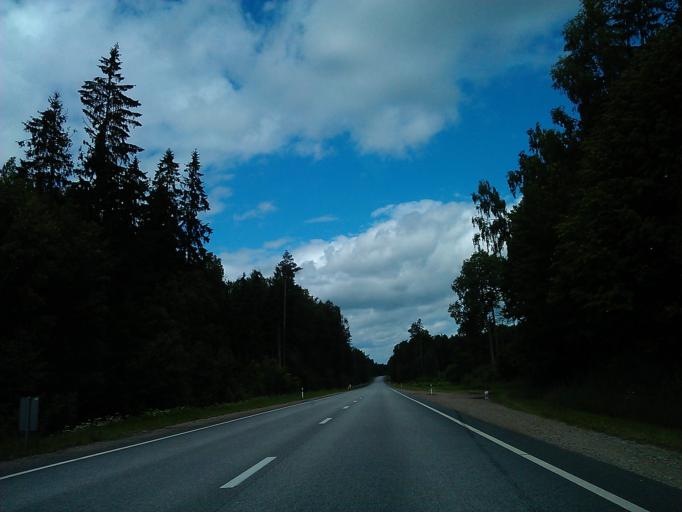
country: LV
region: Tukuma Rajons
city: Tukums
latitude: 56.9921
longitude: 23.0212
